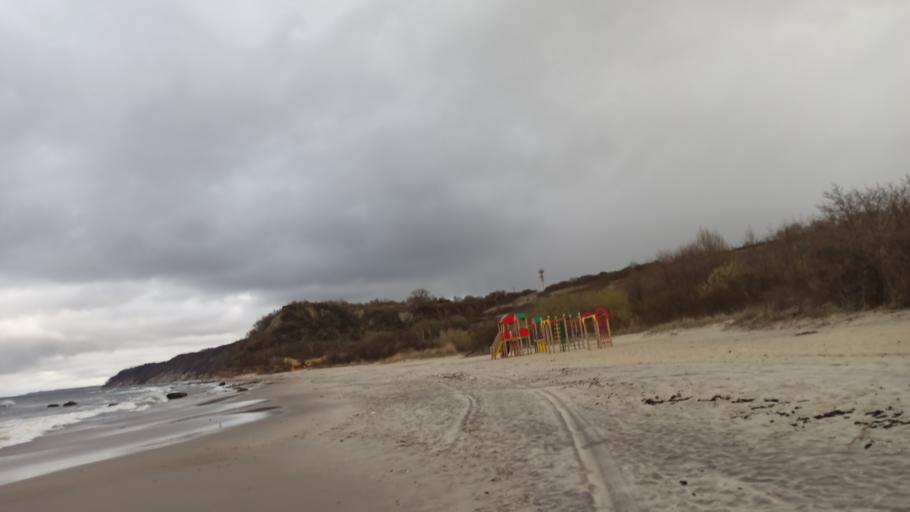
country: RU
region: Kaliningrad
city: Donskoye
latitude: 54.9476
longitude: 20.0210
